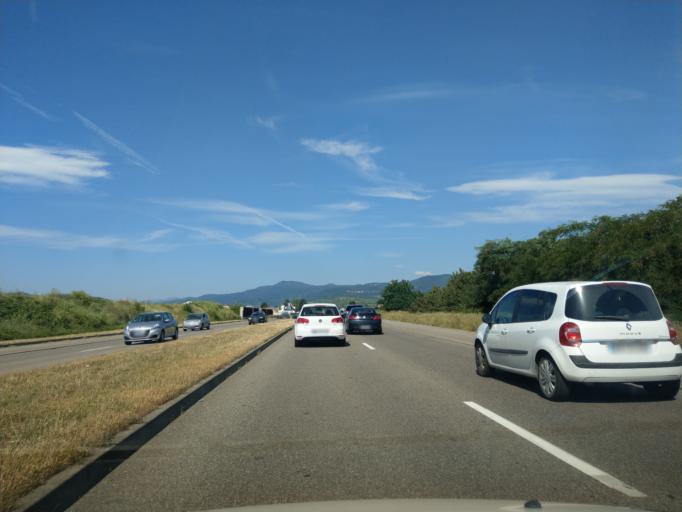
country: FR
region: Alsace
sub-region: Departement du Haut-Rhin
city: Colmar
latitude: 48.0919
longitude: 7.3443
